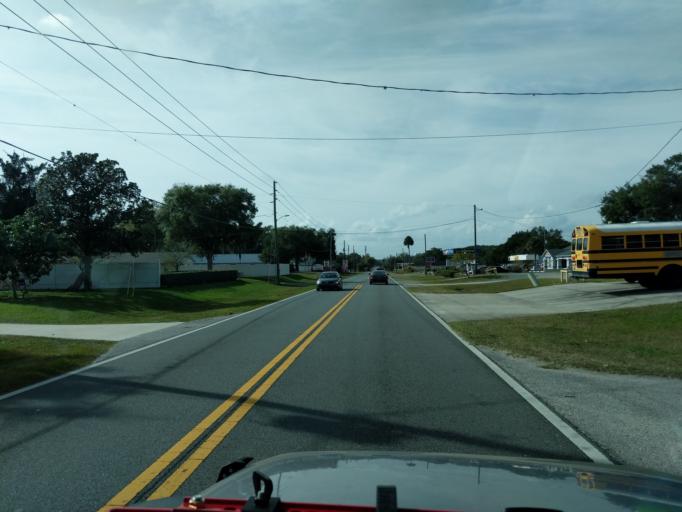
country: US
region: Florida
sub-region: Lake County
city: Tavares
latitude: 28.8040
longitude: -81.7149
